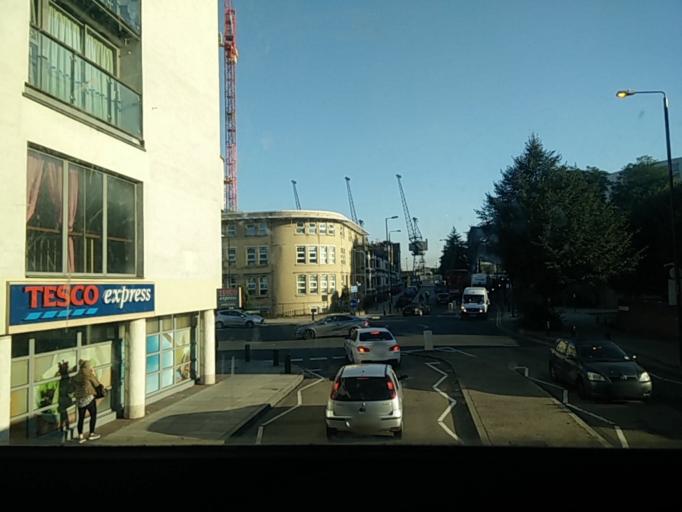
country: GB
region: England
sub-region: Greater London
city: Poplar
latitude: 51.4994
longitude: -0.0094
